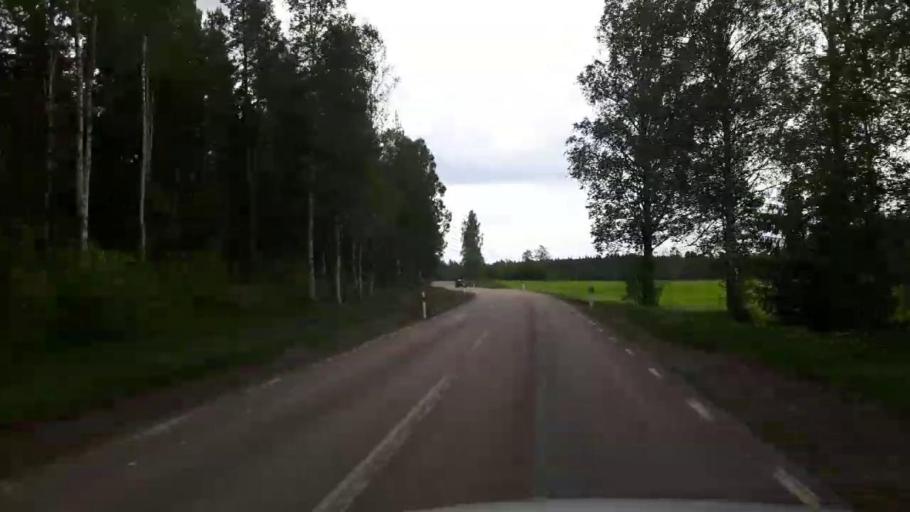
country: SE
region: Vaestmanland
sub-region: Skinnskattebergs Kommun
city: Skinnskatteberg
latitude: 59.8436
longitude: 15.8406
